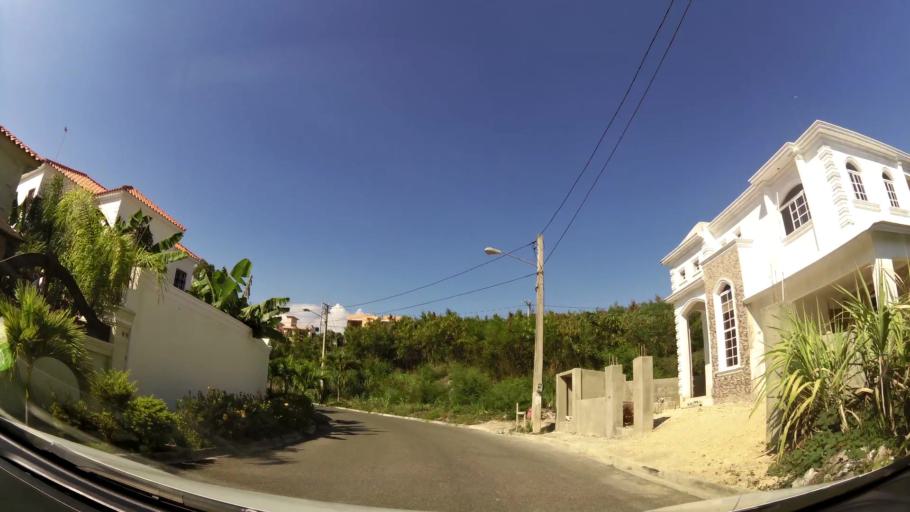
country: DO
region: Nacional
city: Bella Vista
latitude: 18.4593
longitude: -69.9807
